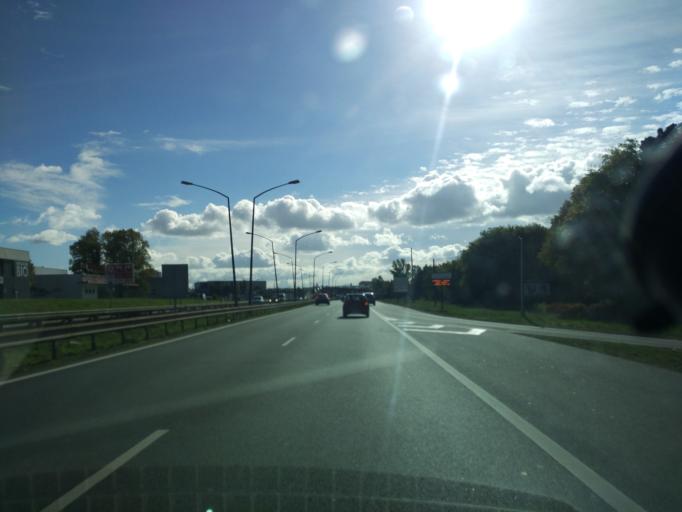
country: FR
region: Aquitaine
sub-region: Departement de la Gironde
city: Le Bouscat
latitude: 44.8731
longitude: -0.5655
